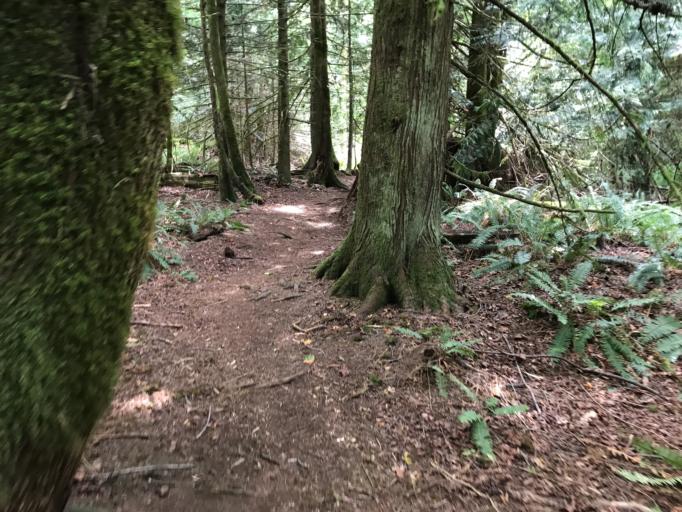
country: CA
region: British Columbia
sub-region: Cowichan Valley Regional District
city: Ladysmith
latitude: 48.9274
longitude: -123.7425
